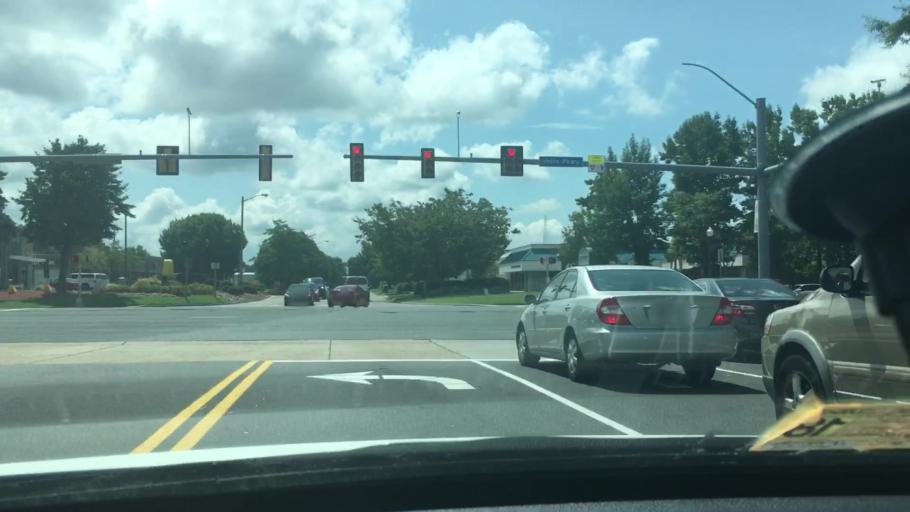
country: US
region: Virginia
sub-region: City of Chesapeake
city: Chesapeake
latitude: 36.7687
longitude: -76.2309
